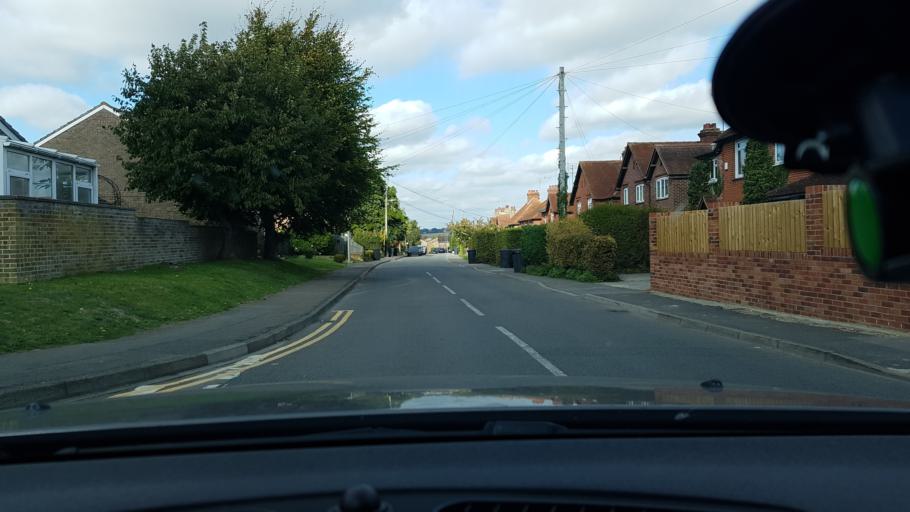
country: GB
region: England
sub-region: West Berkshire
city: Hungerford
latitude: 51.4068
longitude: -1.5175
